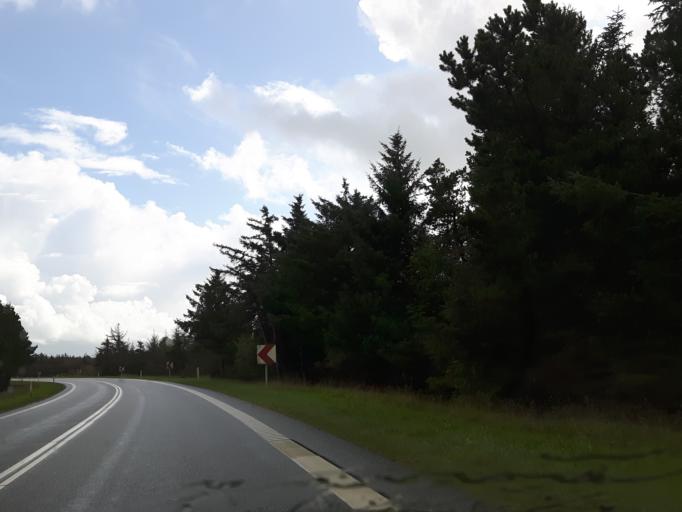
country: DK
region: Central Jutland
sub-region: Struer Kommune
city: Struer
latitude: 56.5867
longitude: 8.5279
